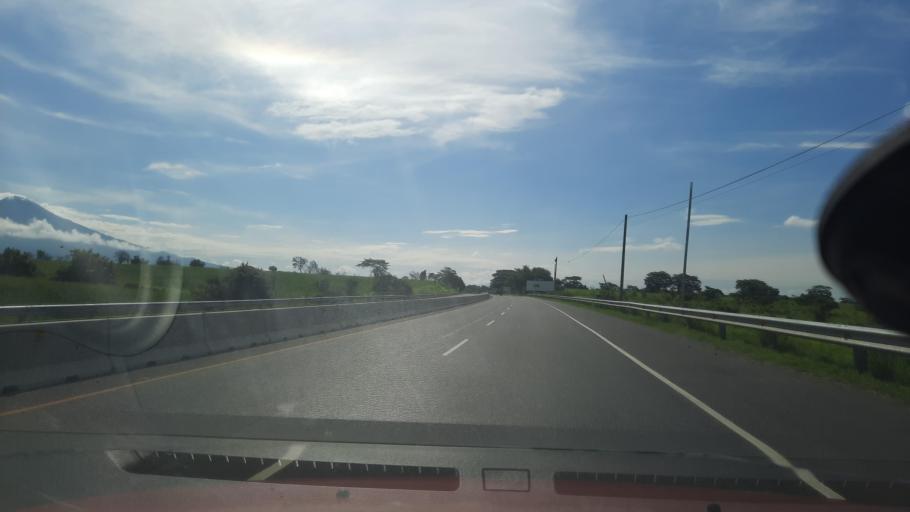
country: SV
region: La Paz
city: Santiago Nonualco
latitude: 13.4852
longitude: -88.9837
